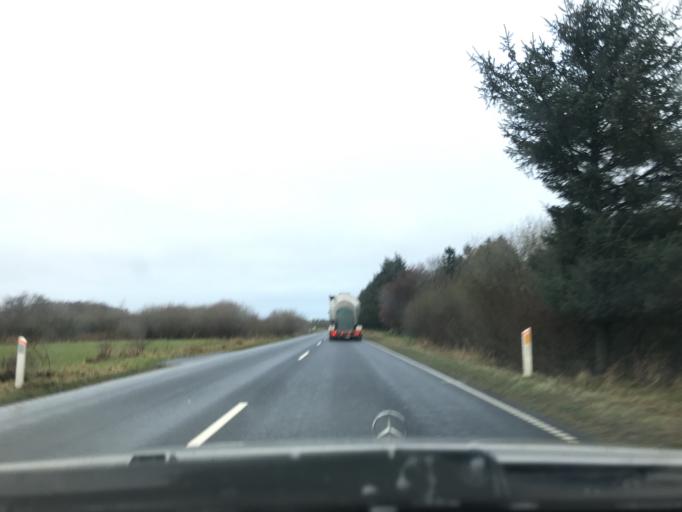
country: DK
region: South Denmark
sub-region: Esbjerg Kommune
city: Ribe
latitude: 55.3076
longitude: 8.7985
